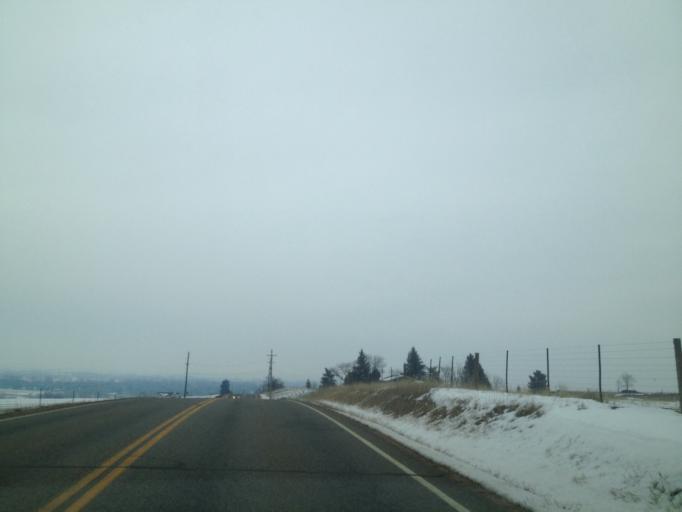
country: US
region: Colorado
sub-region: Boulder County
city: Gunbarrel
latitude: 40.0785
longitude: -105.1691
